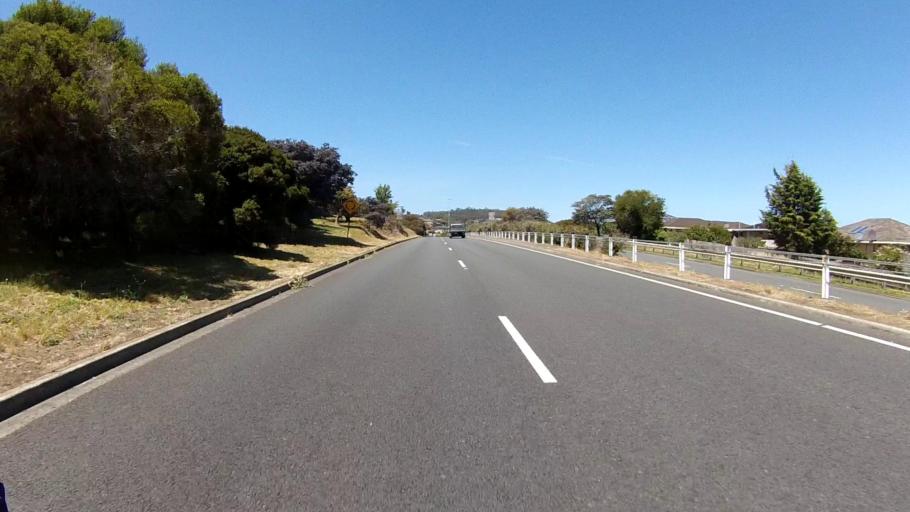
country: AU
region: Tasmania
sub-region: Clarence
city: Howrah
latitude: -42.8761
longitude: 147.4045
